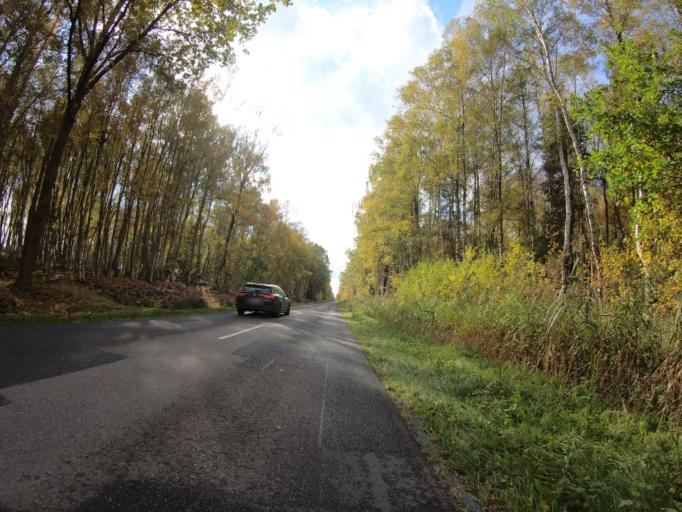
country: DE
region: Lower Saxony
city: Wahrenholz
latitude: 52.5789
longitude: 10.6386
